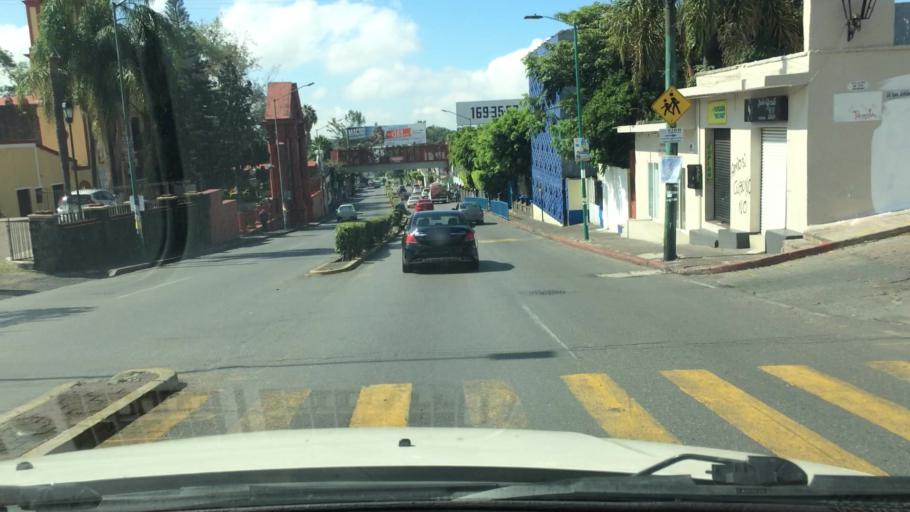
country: MX
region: Morelos
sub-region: Cuernavaca
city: Fraccionamiento Lomas de Ahuatlan
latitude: 18.9476
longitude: -99.2441
